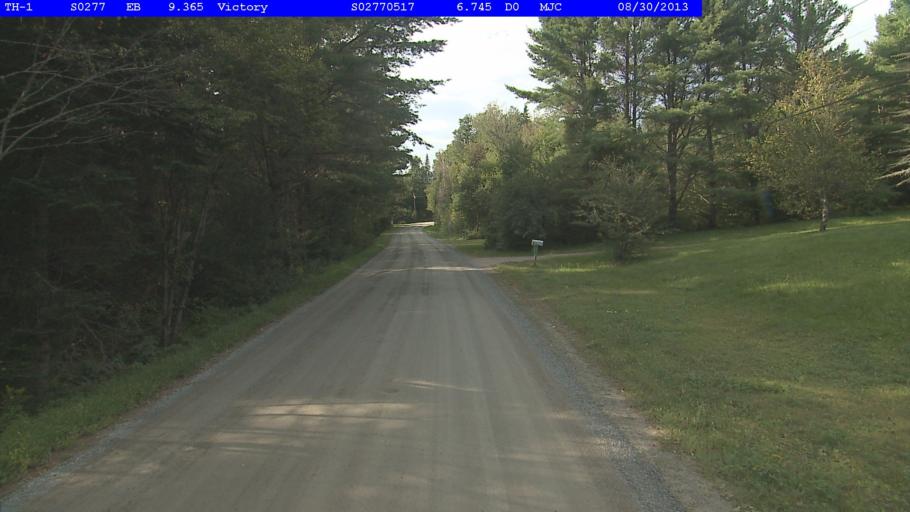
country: US
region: Vermont
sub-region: Caledonia County
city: Lyndonville
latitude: 44.5653
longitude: -71.7881
